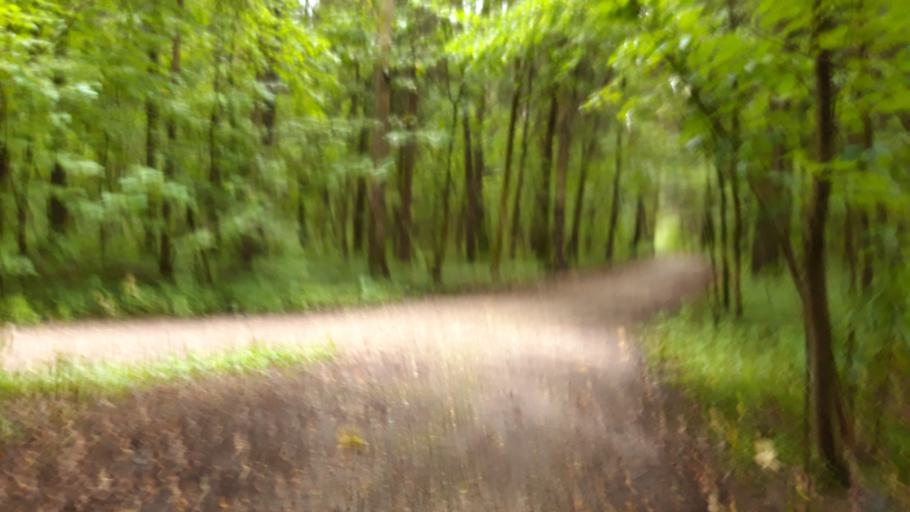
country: RU
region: Moscow
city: Zelenograd
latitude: 55.9863
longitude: 37.2032
